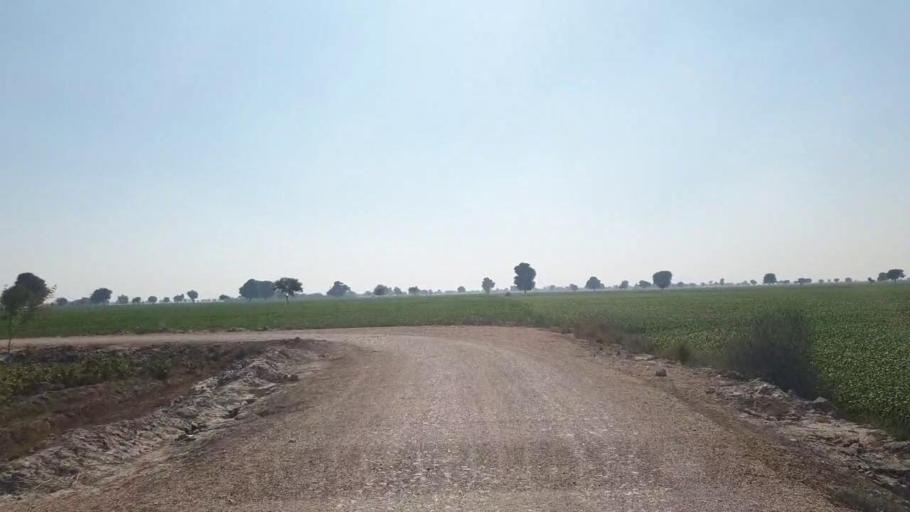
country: PK
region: Sindh
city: Shahpur Chakar
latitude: 26.1038
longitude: 68.6309
